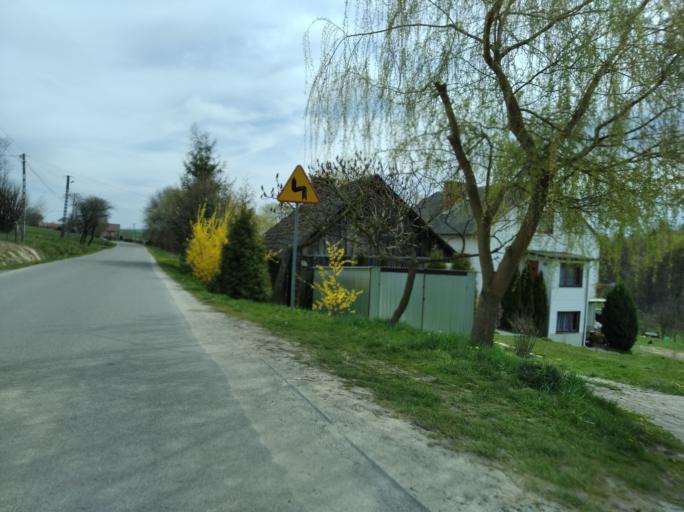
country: PL
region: Subcarpathian Voivodeship
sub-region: Powiat strzyzowski
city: Wisniowa
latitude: 49.9140
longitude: 21.6639
